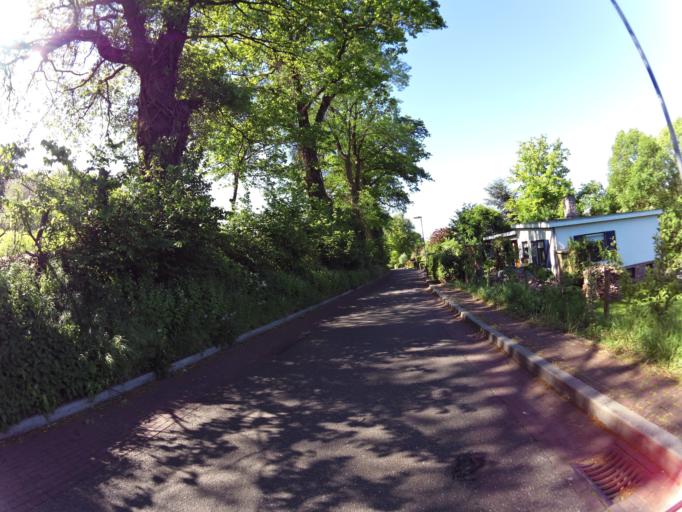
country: NL
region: Limburg
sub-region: Gemeente Schinnen
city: Schinnen
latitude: 50.9382
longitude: 5.8964
